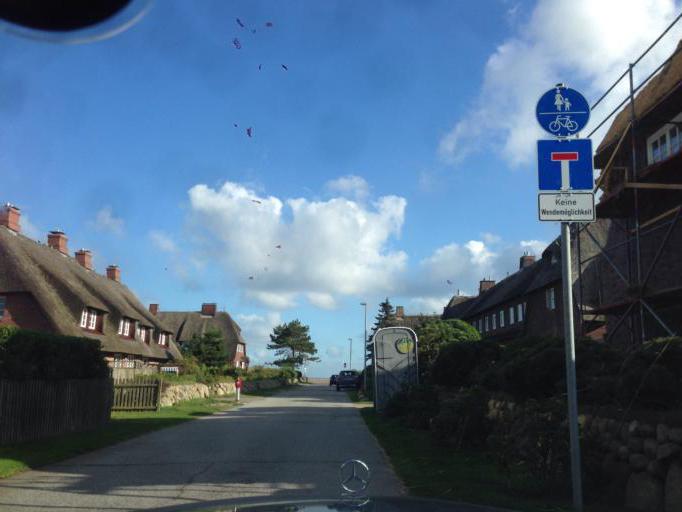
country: DE
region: Schleswig-Holstein
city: List
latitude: 55.0123
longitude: 8.4235
